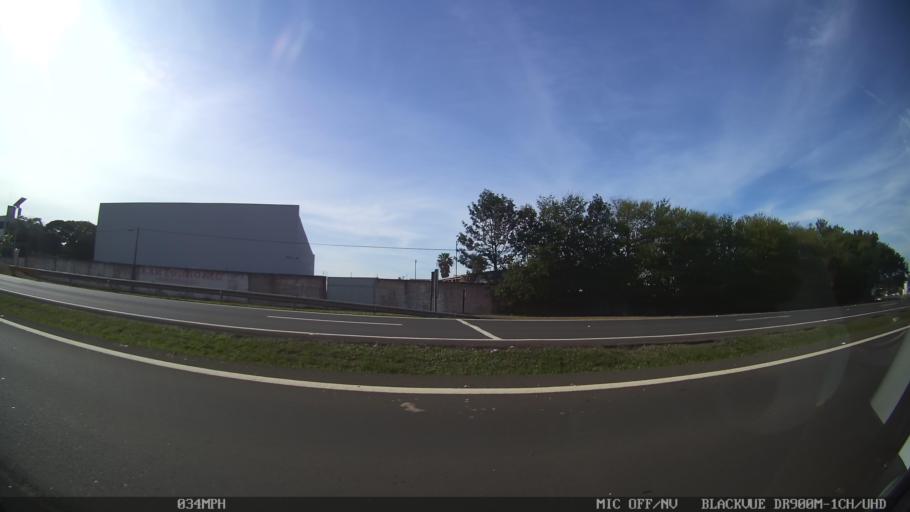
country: BR
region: Sao Paulo
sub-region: Piracicaba
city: Piracicaba
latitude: -22.7651
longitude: -47.6456
